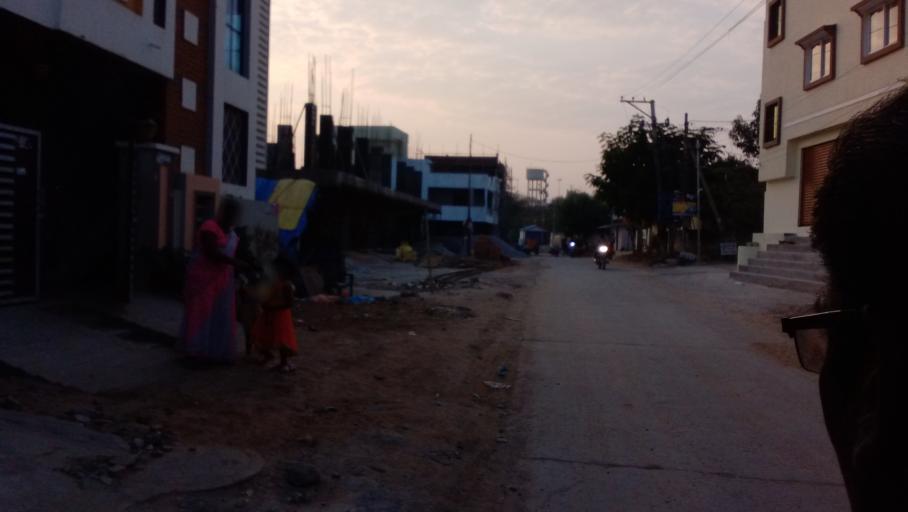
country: IN
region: Telangana
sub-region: Medak
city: Serilingampalle
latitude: 17.5184
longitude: 78.3097
